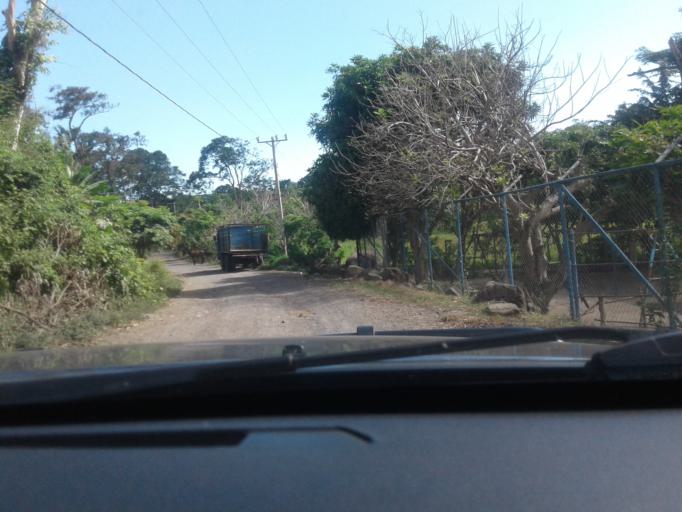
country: NI
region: Rivas
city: Altagracia
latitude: 11.4763
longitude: -85.4680
